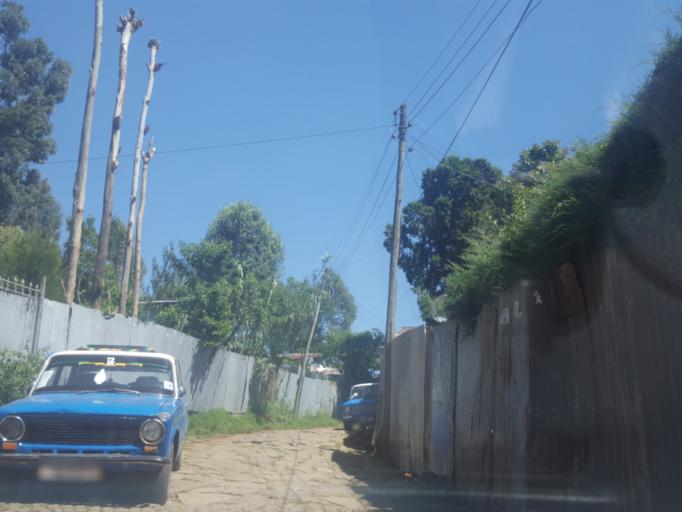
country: ET
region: Adis Abeba
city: Addis Ababa
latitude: 9.0627
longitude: 38.7404
